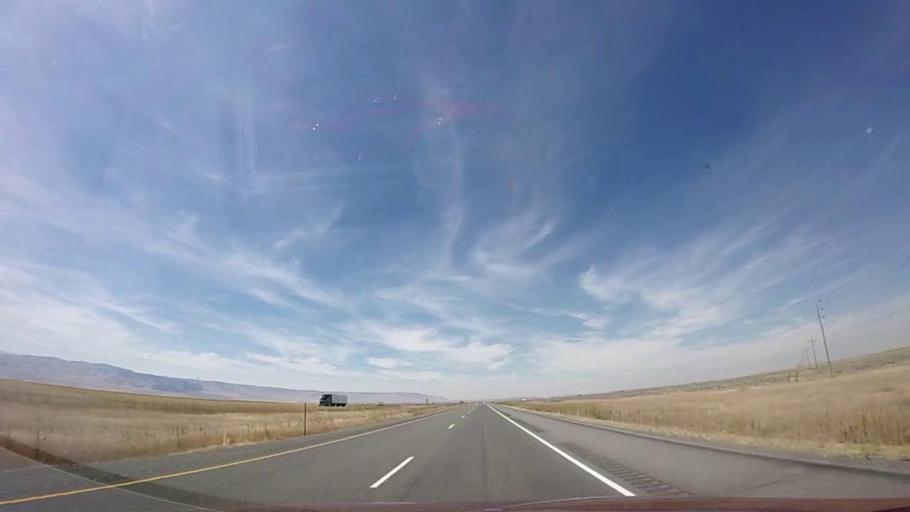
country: US
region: Idaho
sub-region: Minidoka County
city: Rupert
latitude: 42.3605
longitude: -113.2549
